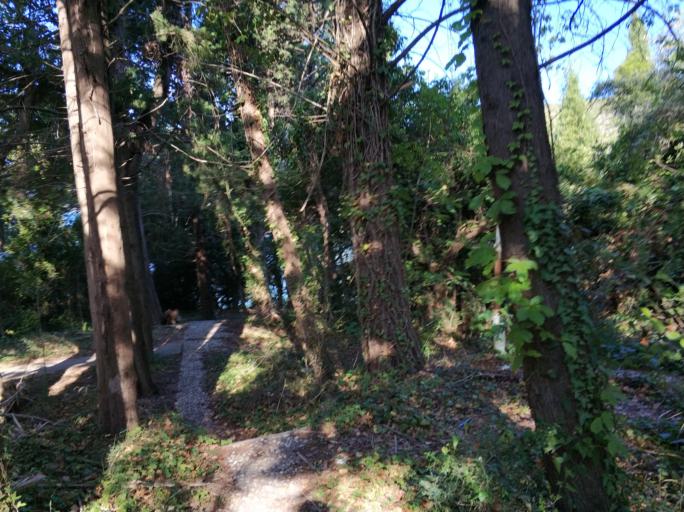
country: ME
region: Budva
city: Budva
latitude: 42.2738
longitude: 18.8889
